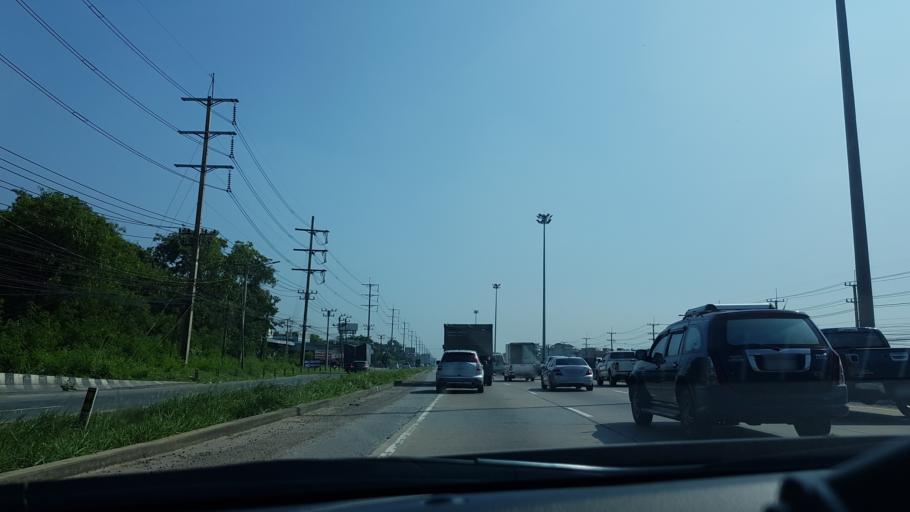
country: TH
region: Phra Nakhon Si Ayutthaya
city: Wang Noi
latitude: 14.2398
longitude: 100.7380
